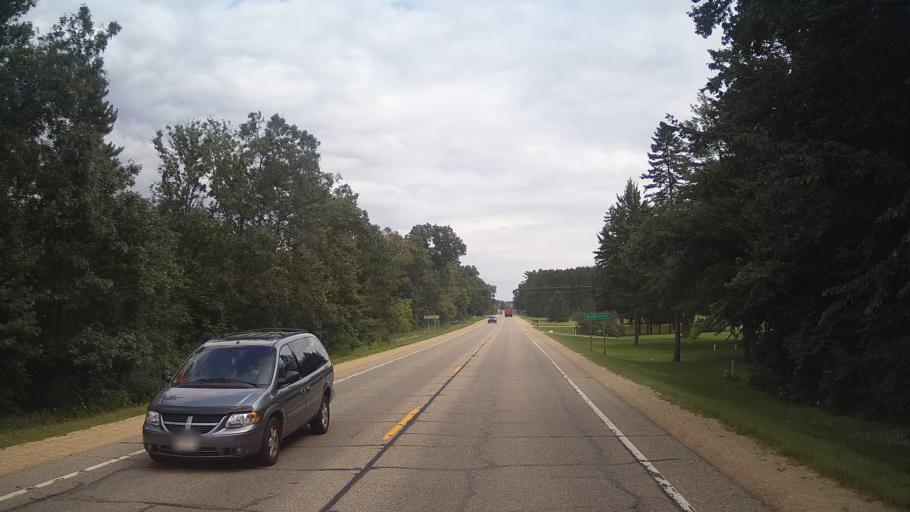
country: US
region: Wisconsin
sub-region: Waushara County
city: Wautoma
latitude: 44.0684
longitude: -89.3141
